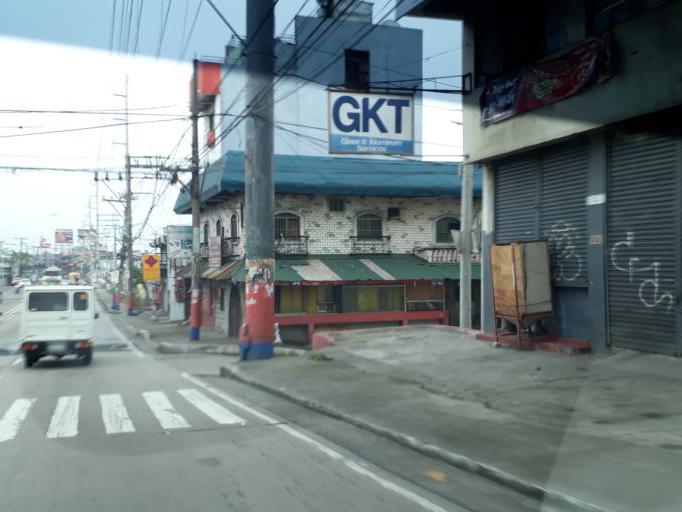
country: PH
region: Metro Manila
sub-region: Caloocan City
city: Niugan
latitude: 14.6694
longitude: 120.9821
